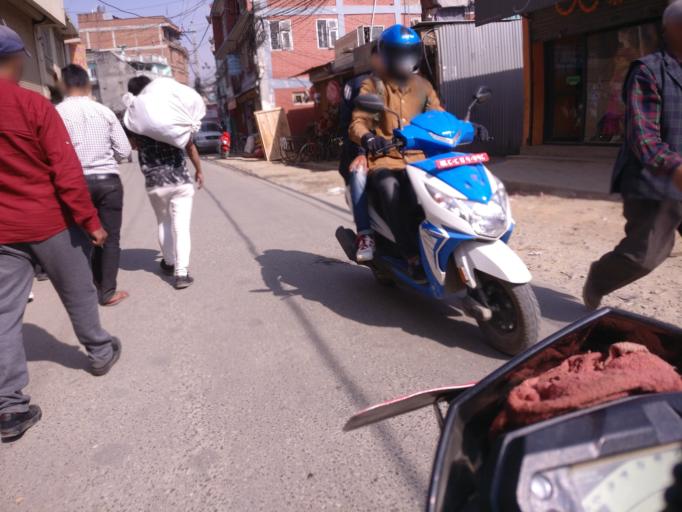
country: NP
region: Central Region
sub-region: Bagmati Zone
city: Patan
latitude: 27.6675
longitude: 85.3246
